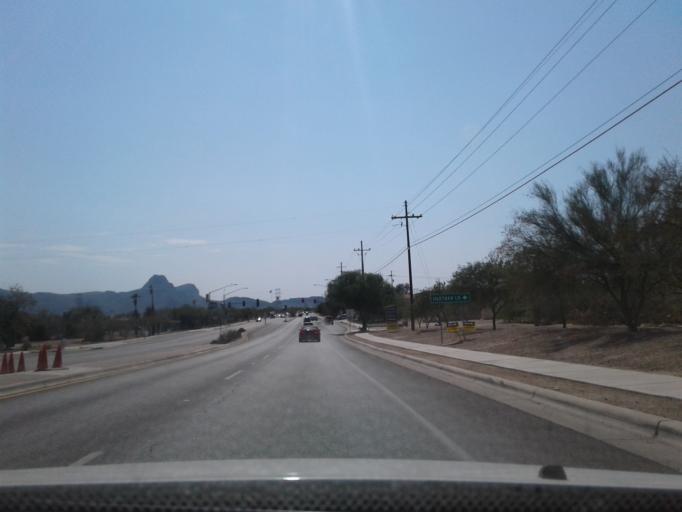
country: US
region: Arizona
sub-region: Pima County
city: Tortolita
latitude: 32.3595
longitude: -111.0784
